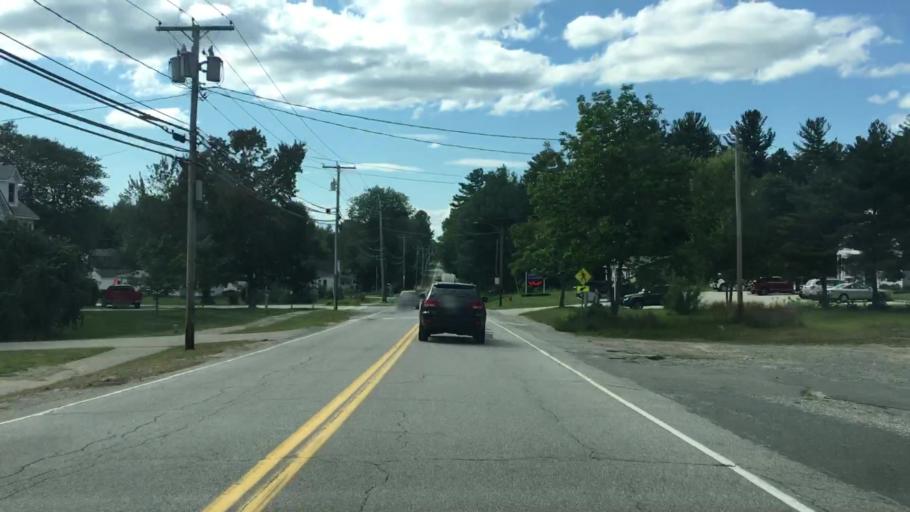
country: US
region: New Hampshire
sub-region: Strafford County
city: Somersworth
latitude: 43.2585
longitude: -70.8715
